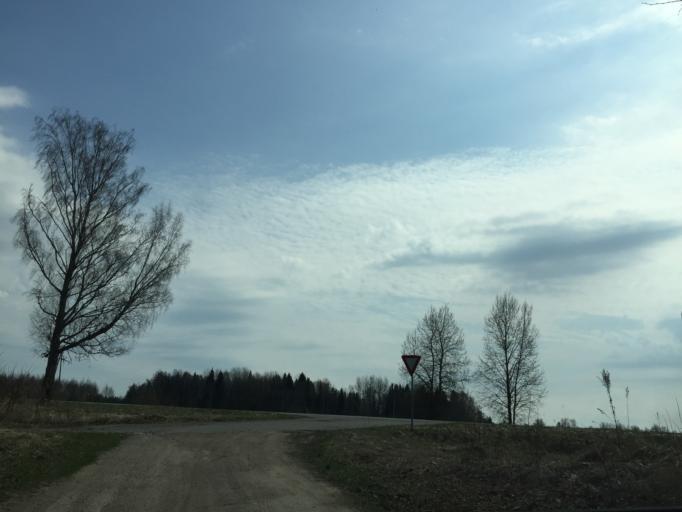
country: LV
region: Apes Novads
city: Ape
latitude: 57.5253
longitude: 26.7802
